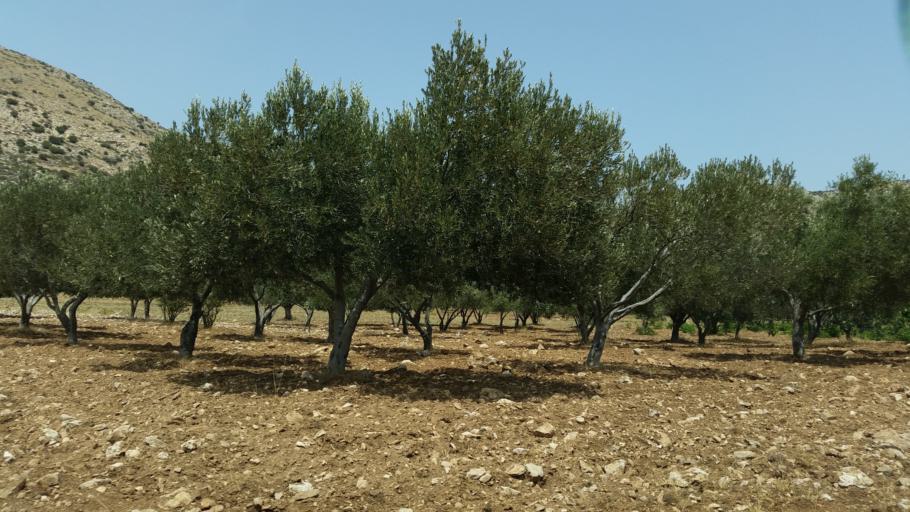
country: GR
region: Attica
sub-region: Nomarchia Anatolikis Attikis
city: Palaia Fokaia
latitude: 37.6737
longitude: 23.9659
